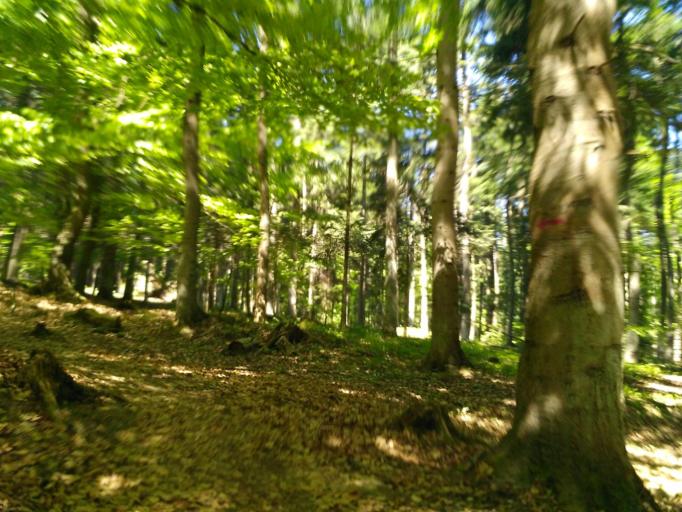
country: PL
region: Subcarpathian Voivodeship
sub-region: Powiat krosnienski
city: Korczyna
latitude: 49.7358
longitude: 21.8578
